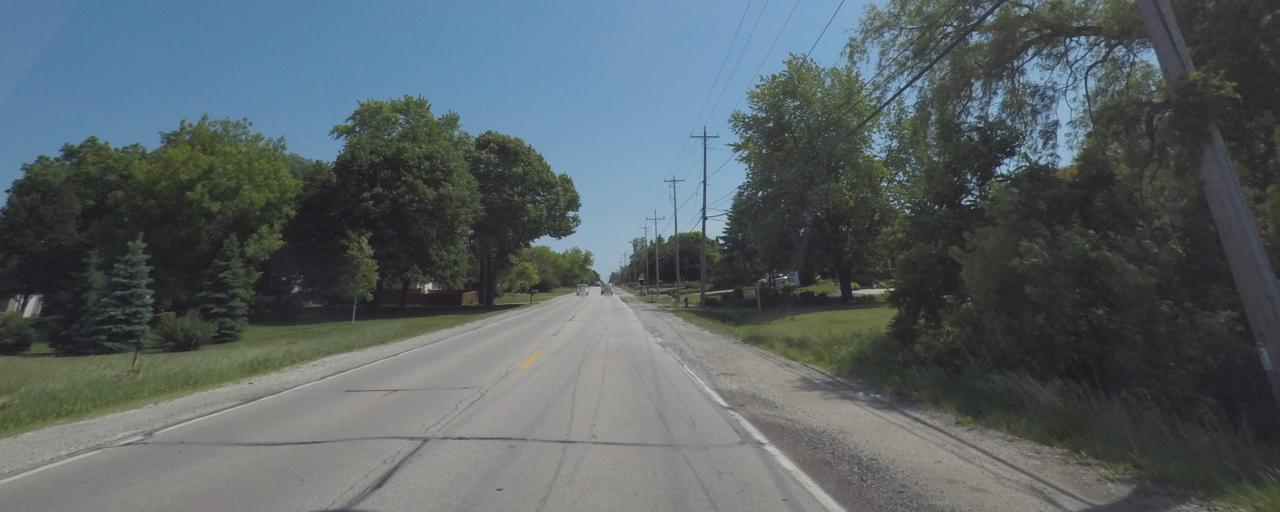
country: US
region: Wisconsin
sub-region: Milwaukee County
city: Oak Creek
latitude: 42.8983
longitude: -87.9314
